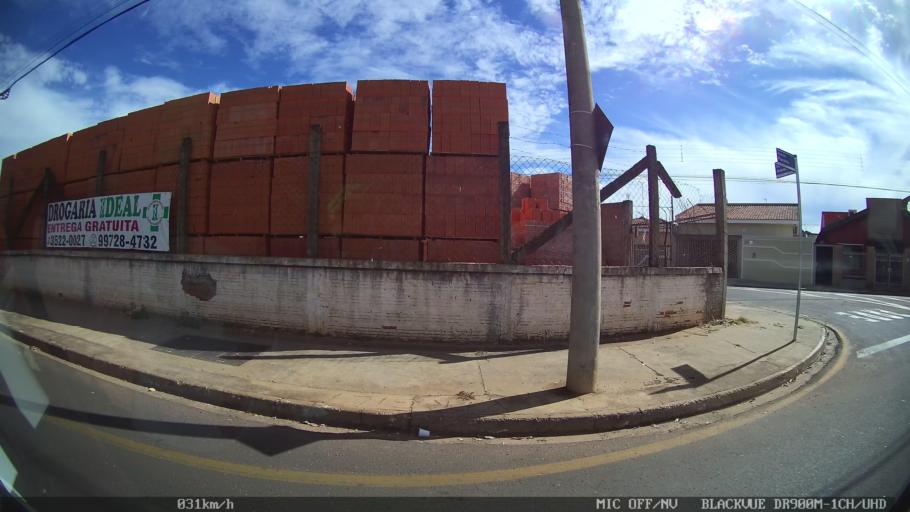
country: BR
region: Sao Paulo
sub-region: Catanduva
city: Catanduva
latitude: -21.1249
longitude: -48.9483
